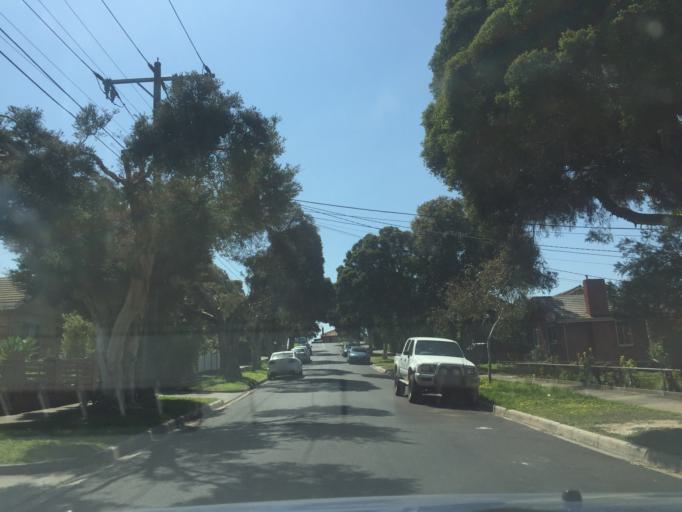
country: AU
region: Victoria
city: Heidelberg West
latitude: -37.7371
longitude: 145.0271
